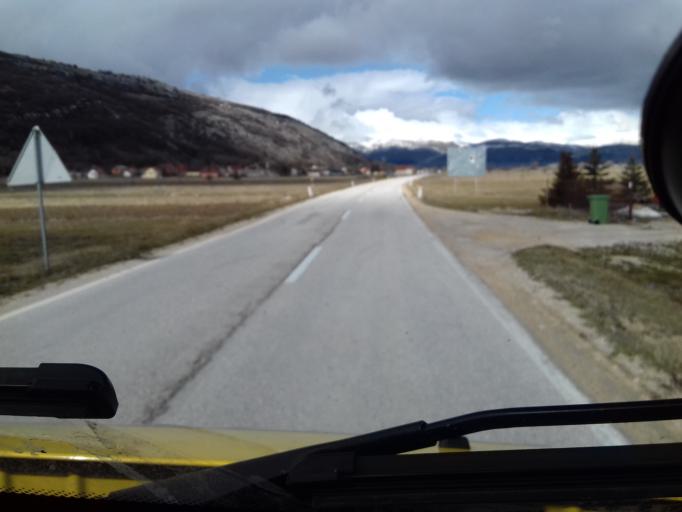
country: BA
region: Federation of Bosnia and Herzegovina
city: Tomislavgrad
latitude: 43.6537
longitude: 17.2181
